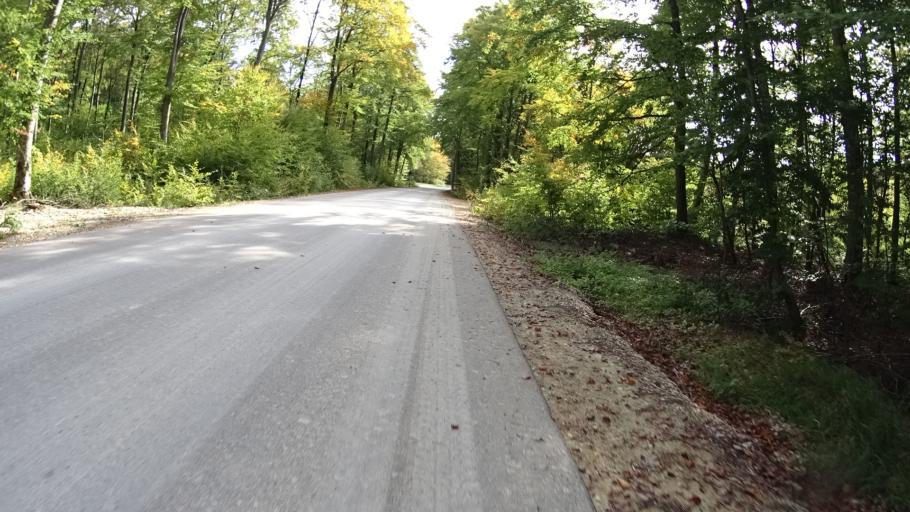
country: DE
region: Bavaria
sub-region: Upper Bavaria
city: Walting
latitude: 48.9063
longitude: 11.3246
